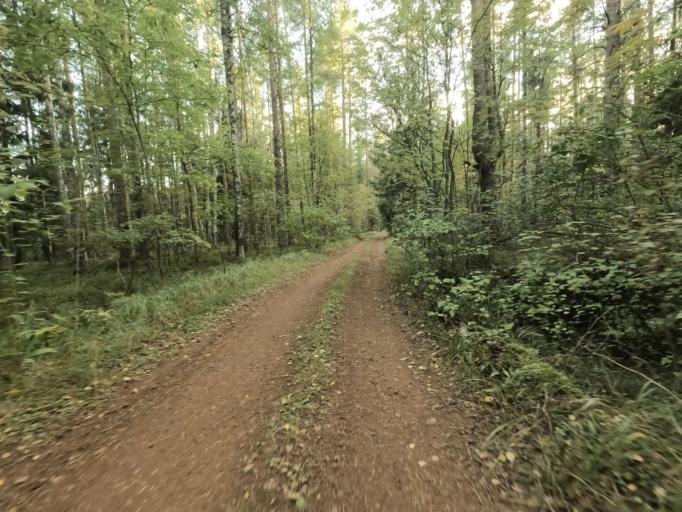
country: RU
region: Leningrad
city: Otradnoye
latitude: 59.8408
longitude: 30.7773
